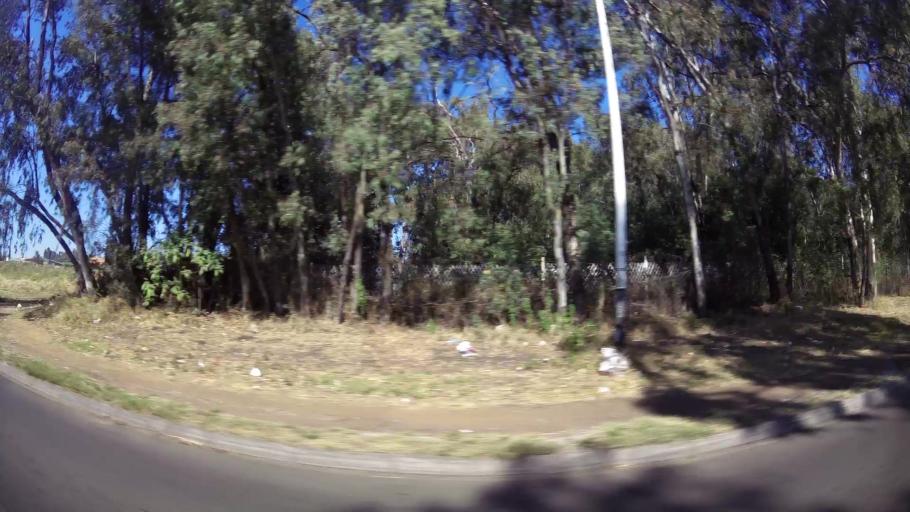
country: ZA
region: Mpumalanga
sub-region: Nkangala District Municipality
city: Witbank
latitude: -25.8597
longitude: 29.2332
